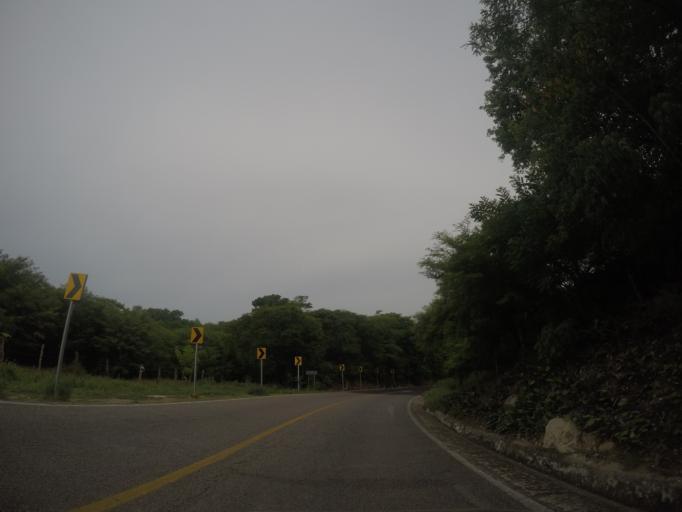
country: MX
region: Oaxaca
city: San Pedro Mixtepec
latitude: 15.9543
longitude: -97.2262
